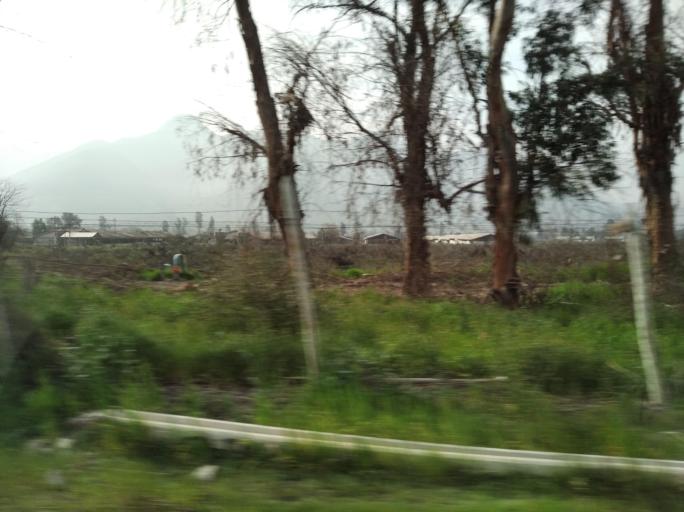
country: CL
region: Santiago Metropolitan
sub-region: Provincia de Chacabuco
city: Lampa
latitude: -33.2296
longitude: -70.9247
